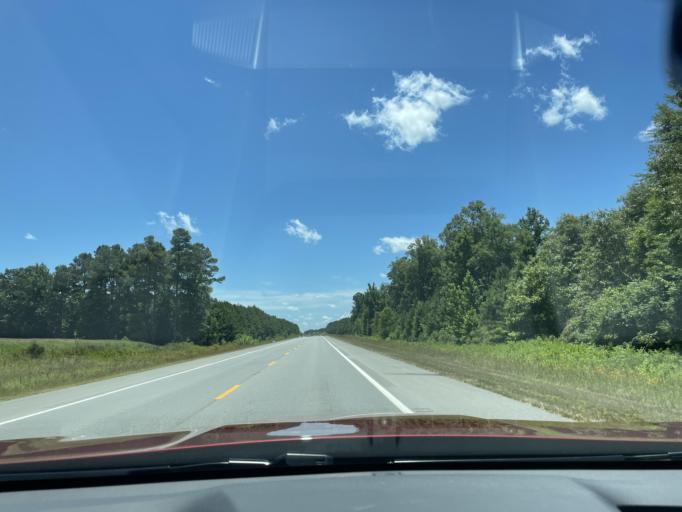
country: US
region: Arkansas
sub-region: Lincoln County
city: Star City
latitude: 33.9675
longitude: -91.9131
